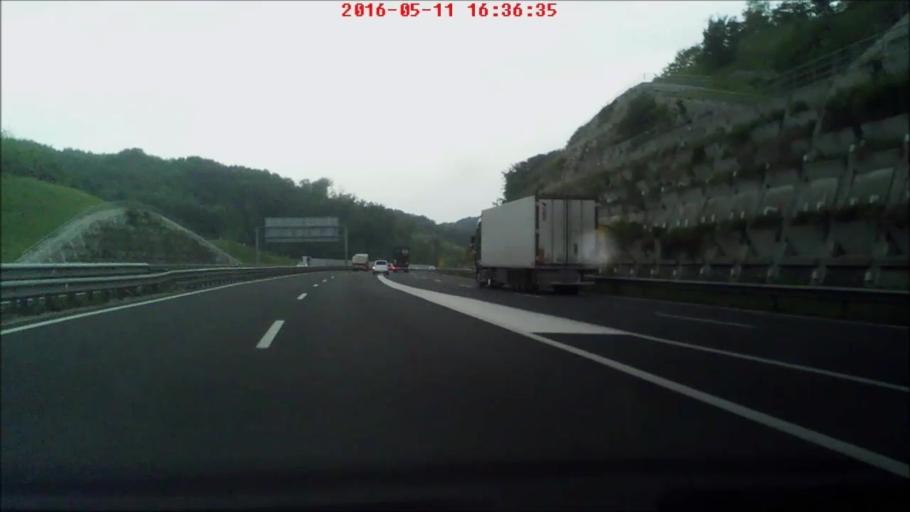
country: SI
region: Pesnica
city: Pesnica pri Mariboru
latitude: 46.5827
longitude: 15.6893
